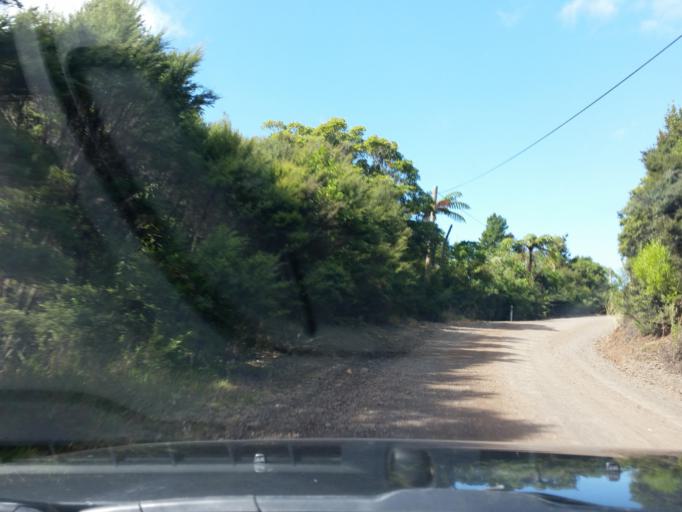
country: NZ
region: Northland
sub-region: Kaipara District
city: Dargaville
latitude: -35.7160
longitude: 173.5512
